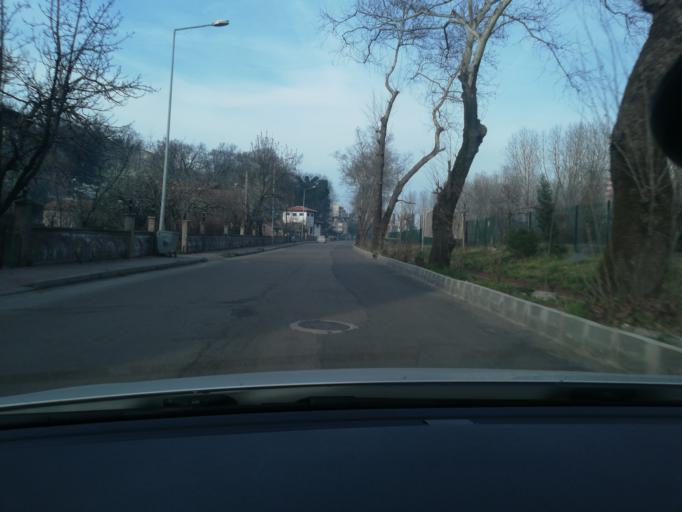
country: TR
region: Zonguldak
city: Kilimli
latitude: 41.5075
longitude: 31.8870
